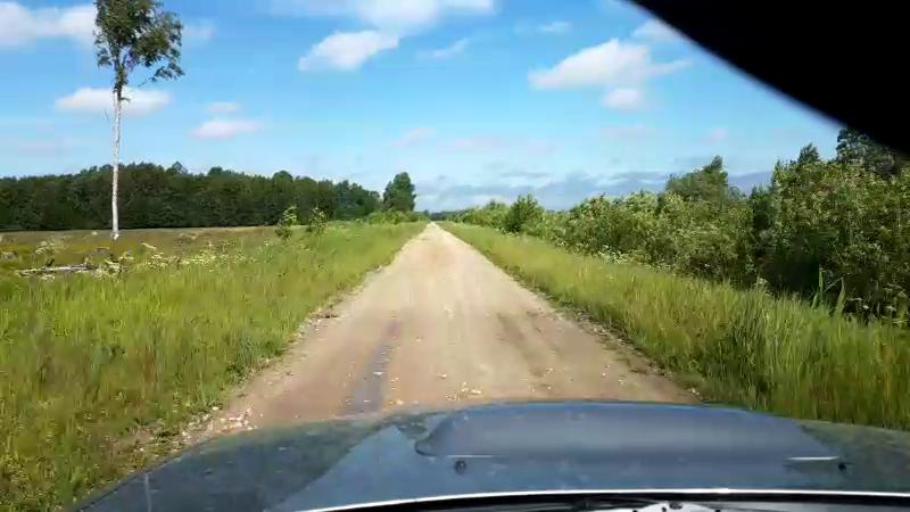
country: EE
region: Paernumaa
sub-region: Sindi linn
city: Sindi
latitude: 58.4890
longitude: 24.6576
